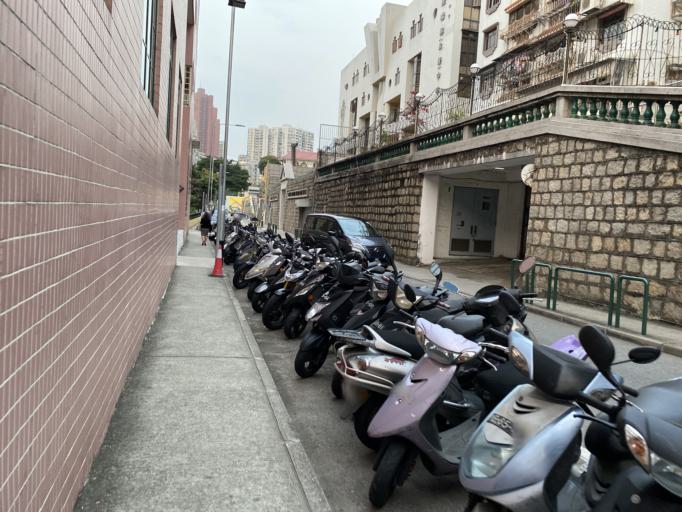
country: MO
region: Macau
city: Macau
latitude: 22.1980
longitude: 113.5487
